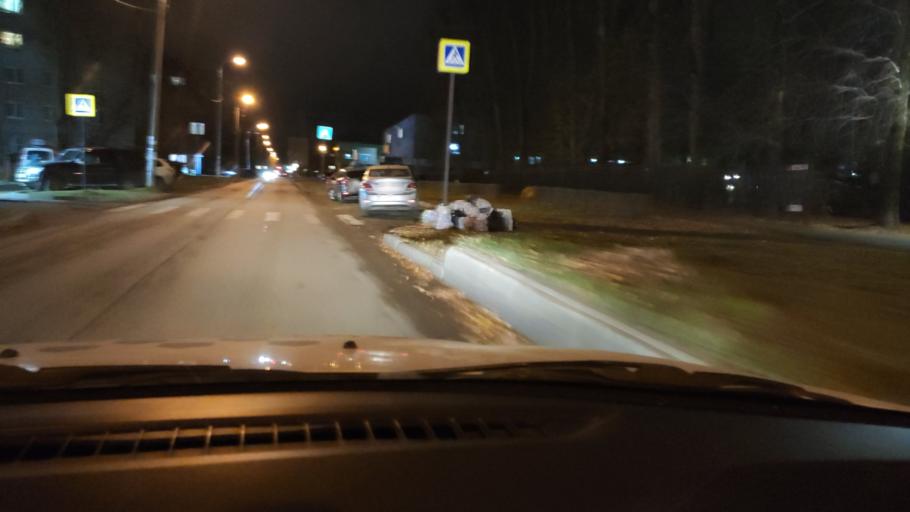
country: RU
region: Perm
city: Perm
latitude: 57.9837
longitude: 56.2090
